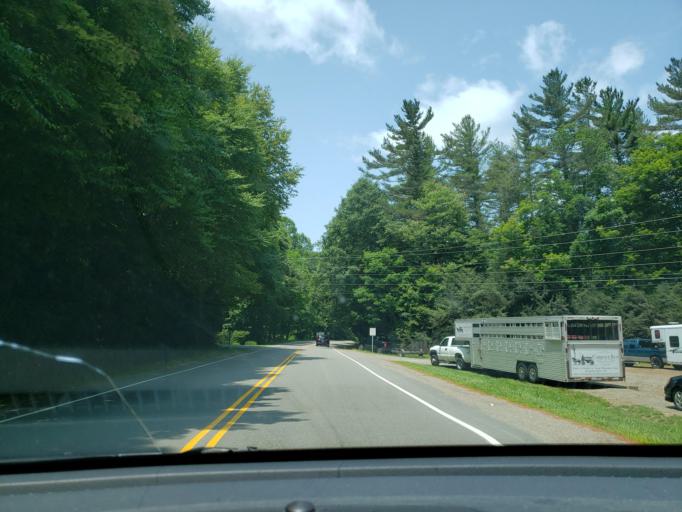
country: US
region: North Carolina
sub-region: Watauga County
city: Blowing Rock
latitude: 36.1387
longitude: -81.6869
